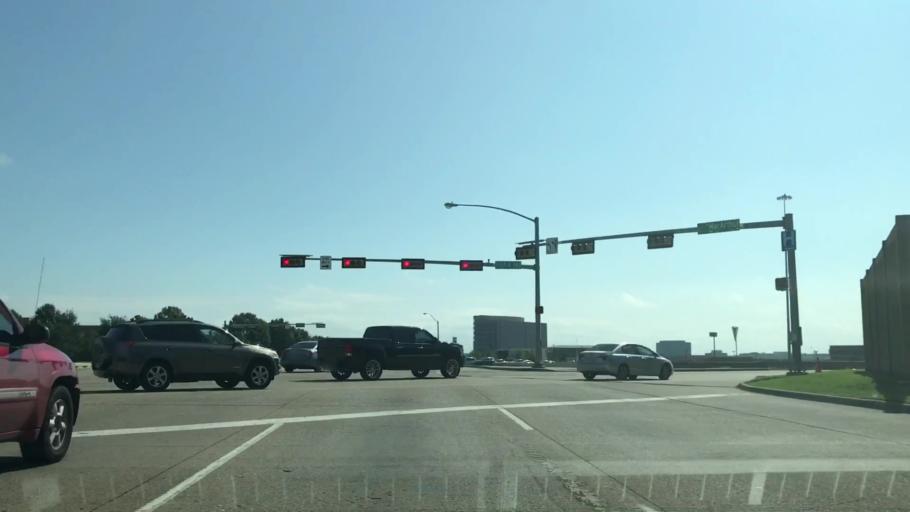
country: US
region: Texas
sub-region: Dallas County
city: Farmers Branch
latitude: 32.9053
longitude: -96.9589
